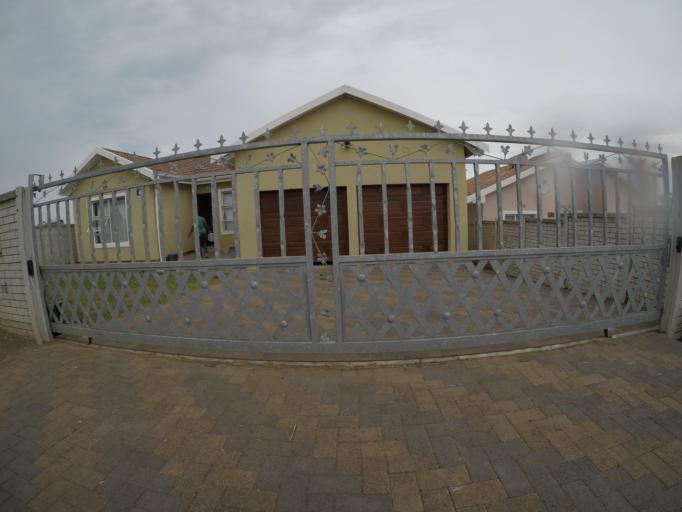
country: ZA
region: Eastern Cape
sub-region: Buffalo City Metropolitan Municipality
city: East London
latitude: -32.9970
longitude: 27.8537
